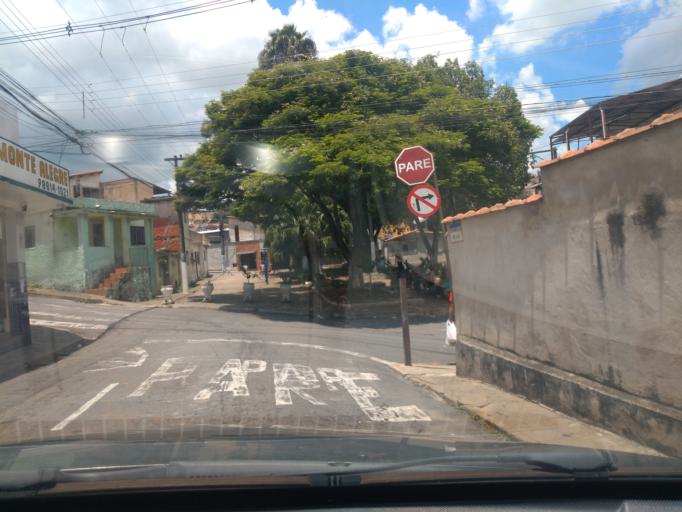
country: BR
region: Minas Gerais
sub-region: Tres Coracoes
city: Tres Coracoes
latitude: -21.6912
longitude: -45.2560
